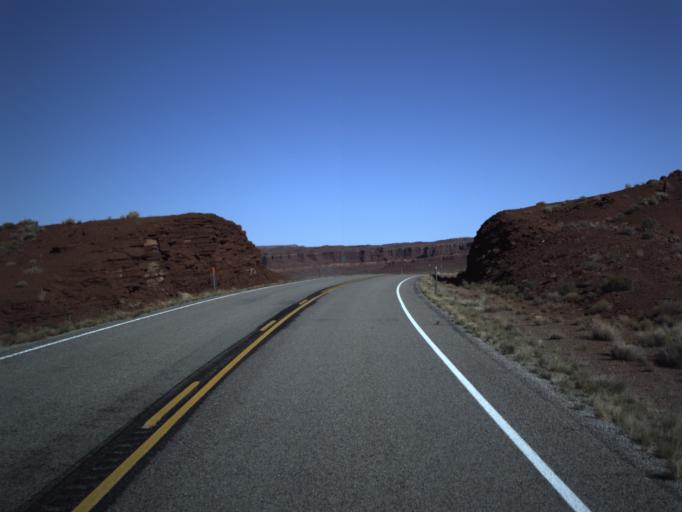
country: US
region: Utah
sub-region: San Juan County
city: Blanding
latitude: 37.8255
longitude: -110.3586
